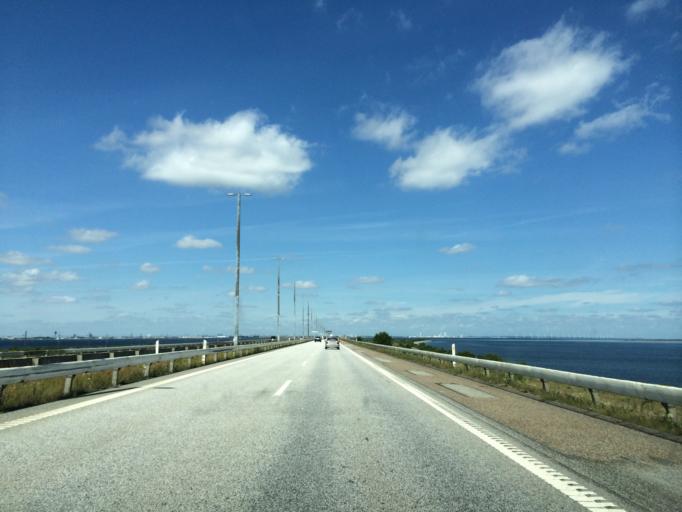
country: DK
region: Capital Region
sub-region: Dragor Kommune
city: Dragor
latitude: 55.5962
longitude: 12.7601
